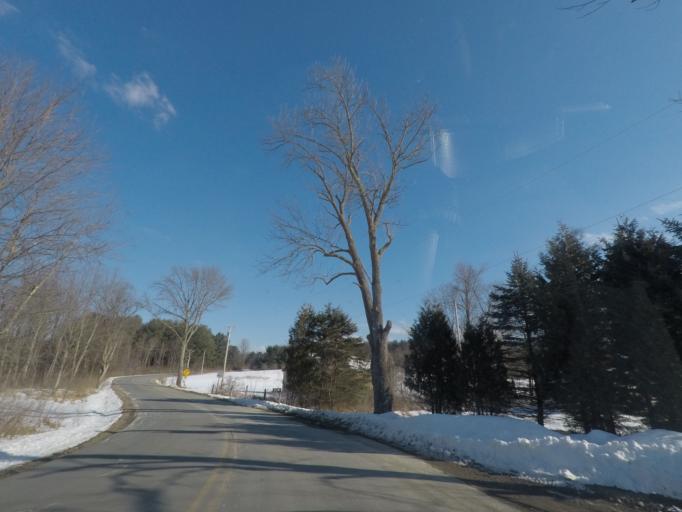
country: US
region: New York
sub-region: Rensselaer County
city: Hoosick Falls
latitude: 42.8960
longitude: -73.5016
